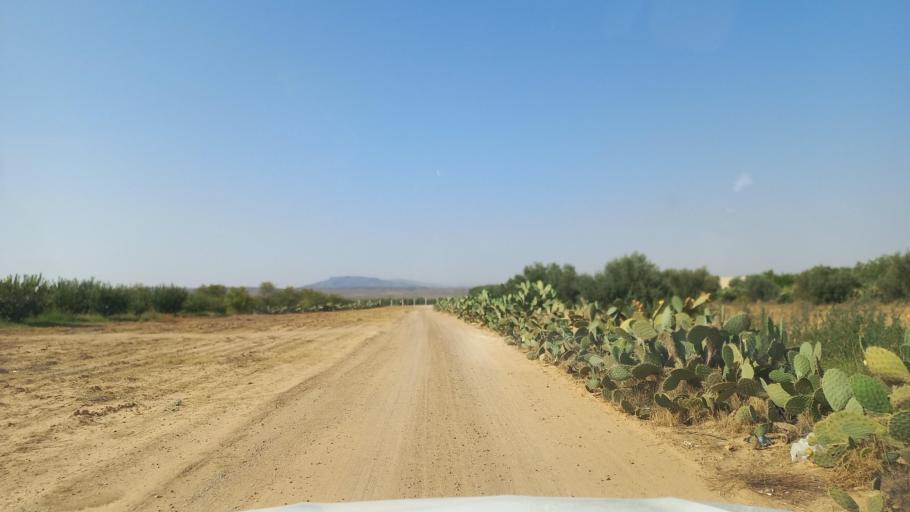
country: TN
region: Al Qasrayn
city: Kasserine
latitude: 35.2438
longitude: 9.0289
